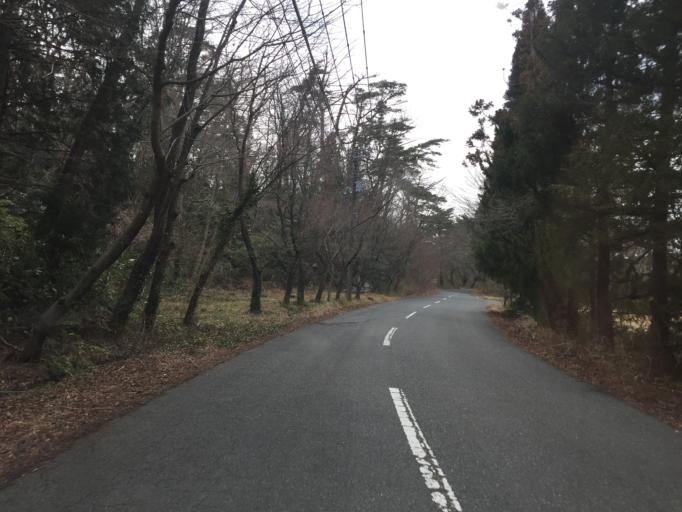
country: JP
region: Ibaraki
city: Kitaibaraki
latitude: 36.8707
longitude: 140.7824
